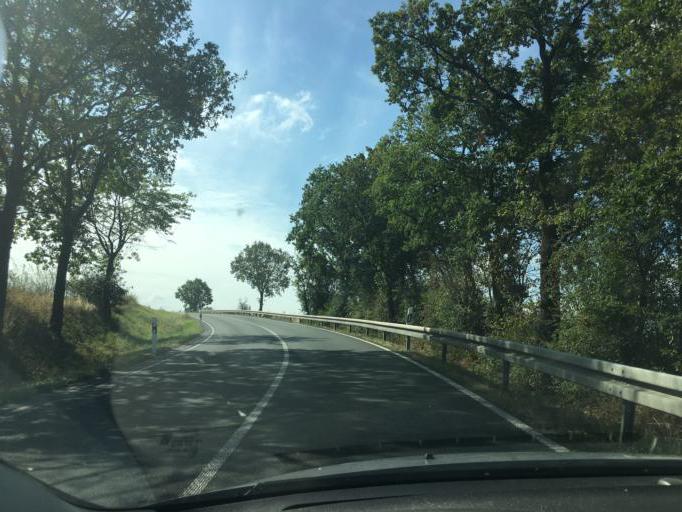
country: DE
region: Thuringia
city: Mittelpollnitz
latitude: 50.7412
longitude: 11.9114
